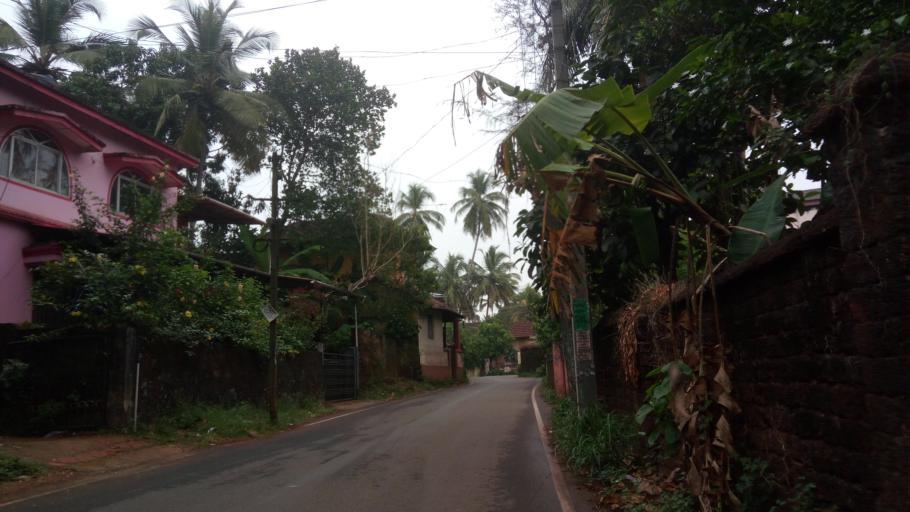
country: IN
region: Kerala
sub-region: Malappuram
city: Malappuram
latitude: 10.9952
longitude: 76.0102
